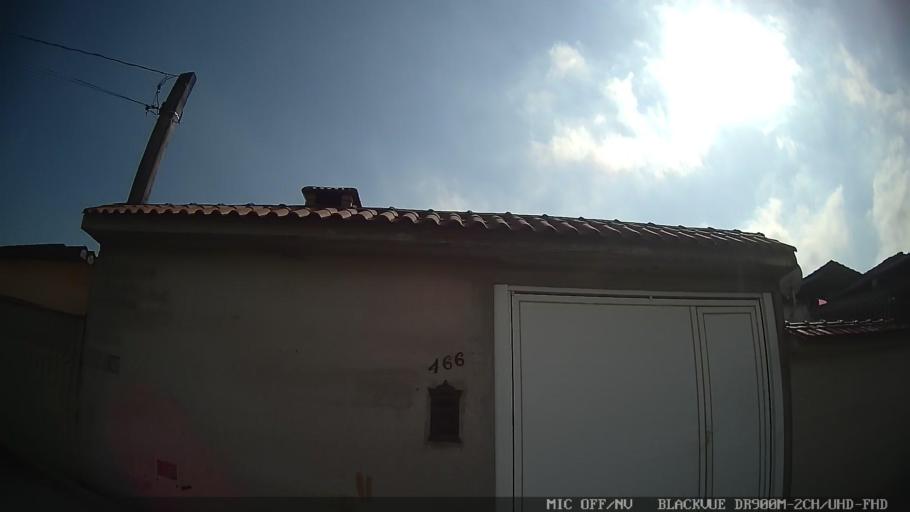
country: BR
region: Sao Paulo
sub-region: Santos
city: Santos
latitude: -23.9475
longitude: -46.3031
